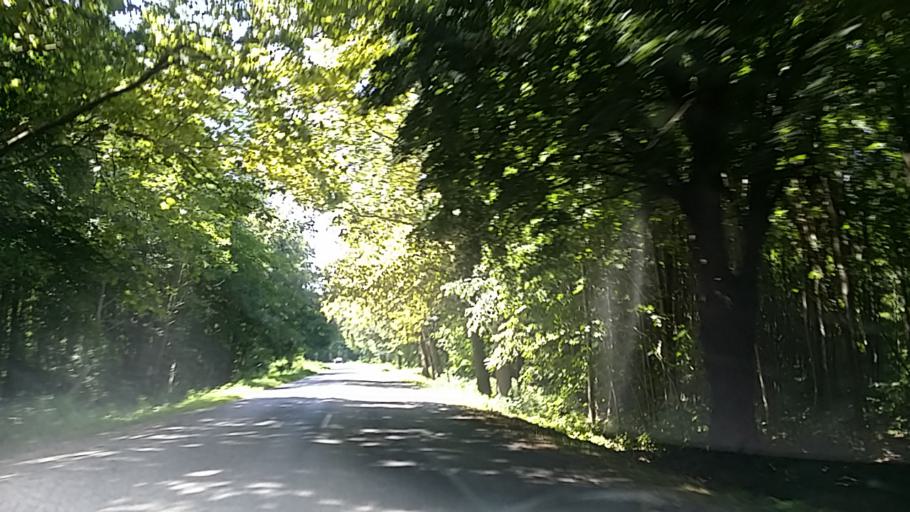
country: HU
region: Somogy
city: Balatonlelle
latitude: 46.7378
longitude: 17.7598
